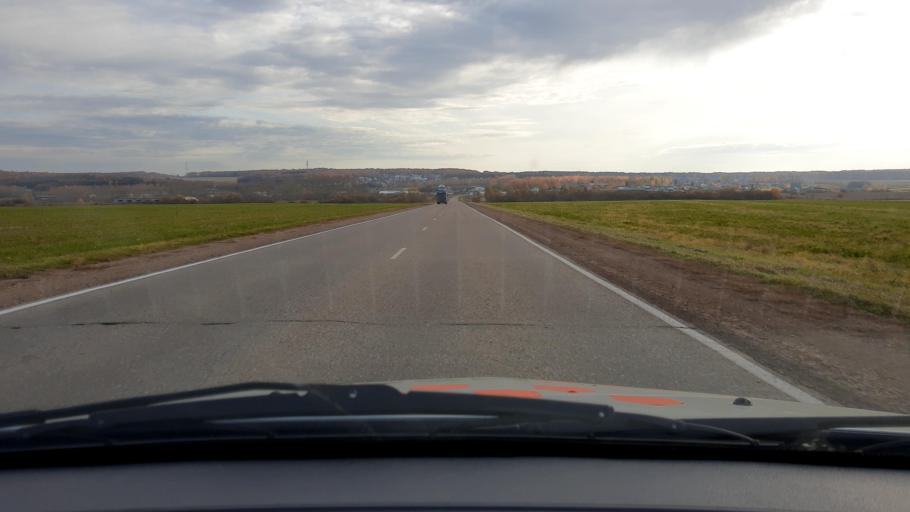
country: RU
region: Bashkortostan
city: Avdon
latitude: 54.8218
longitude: 55.6698
